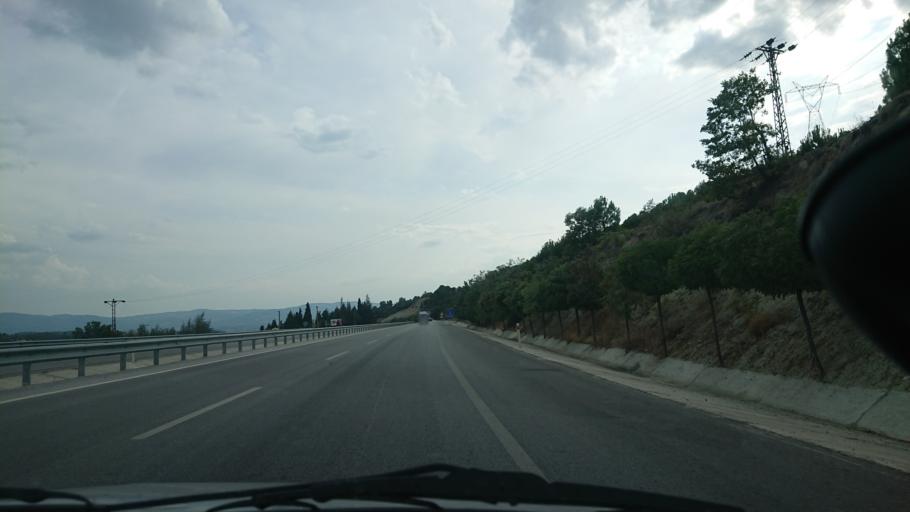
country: TR
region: Kuetahya
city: Gediz
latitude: 39.0265
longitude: 29.4161
